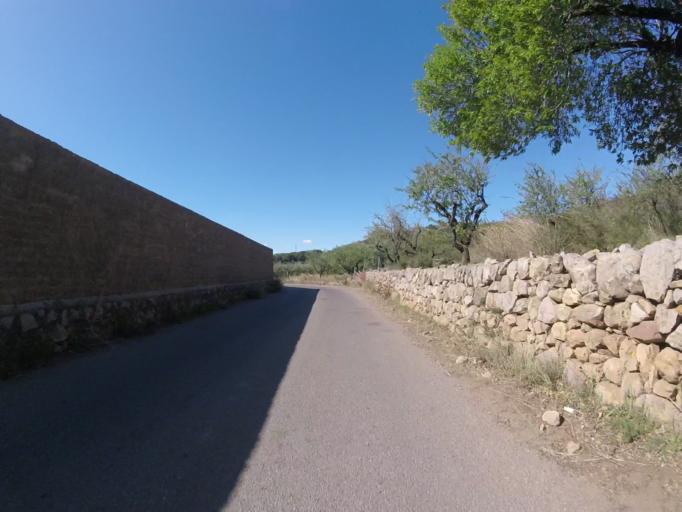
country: ES
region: Valencia
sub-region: Provincia de Castello
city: Benicassim
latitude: 40.0682
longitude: 0.0746
